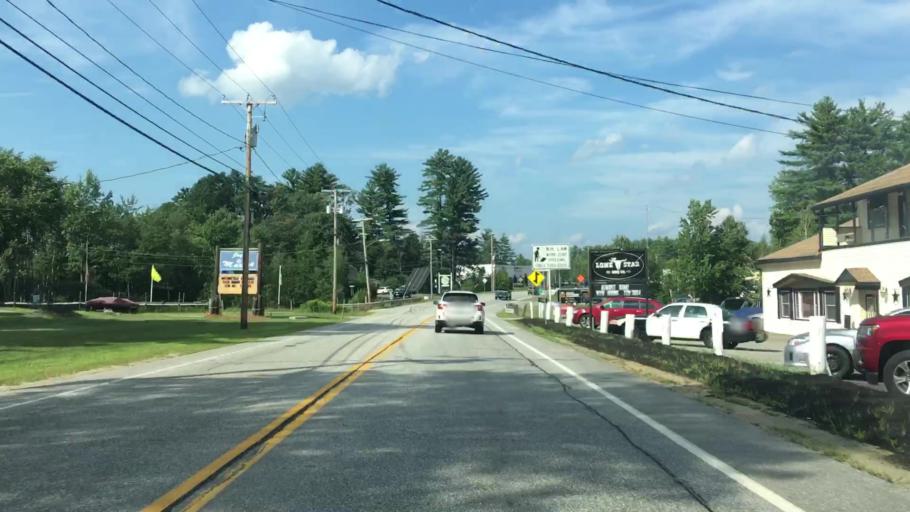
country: US
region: New Hampshire
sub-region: Belknap County
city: Laconia
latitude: 43.4978
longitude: -71.5189
